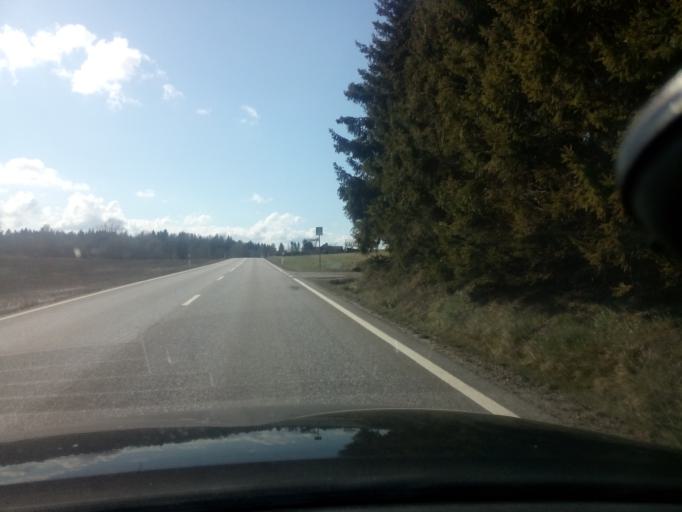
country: SE
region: Soedermanland
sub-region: Flens Kommun
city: Malmkoping
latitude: 59.1029
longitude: 16.7829
